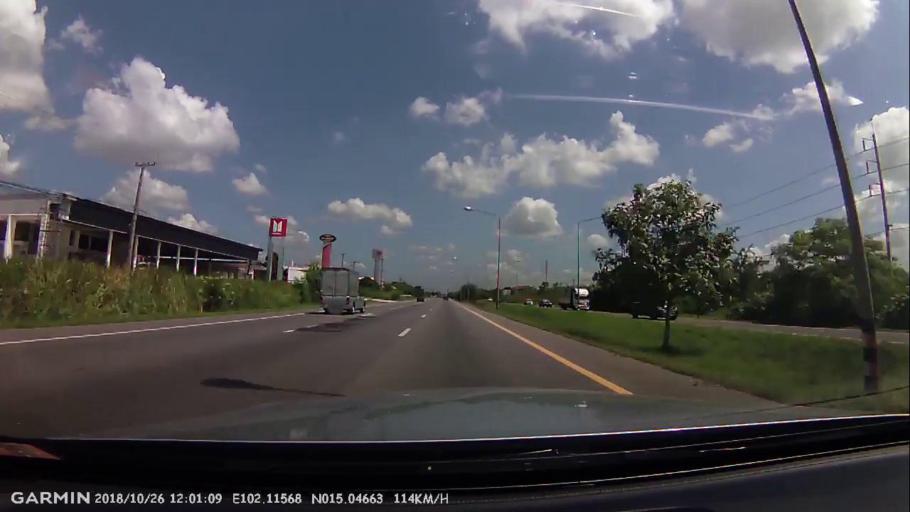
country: TH
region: Nakhon Ratchasima
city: Nakhon Ratchasima
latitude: 15.0467
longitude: 102.1158
